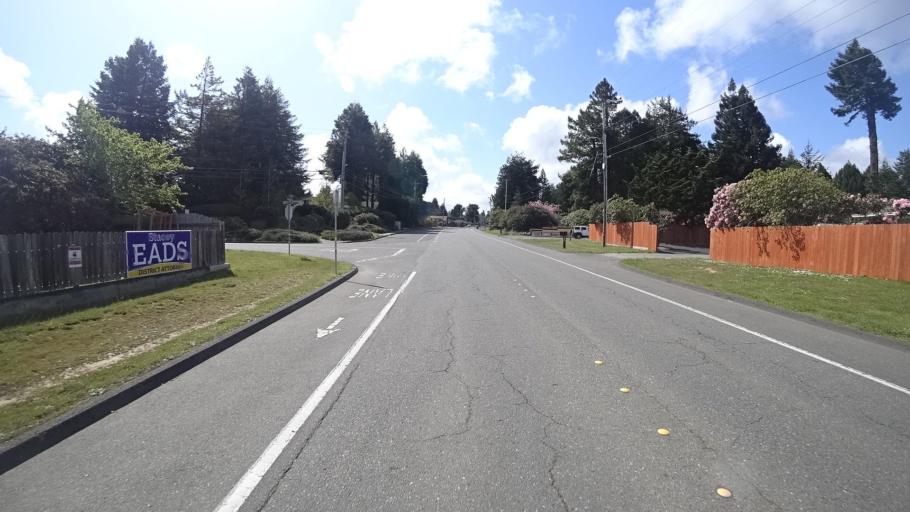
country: US
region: California
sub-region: Humboldt County
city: Pine Hills
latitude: 40.7455
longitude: -124.1477
